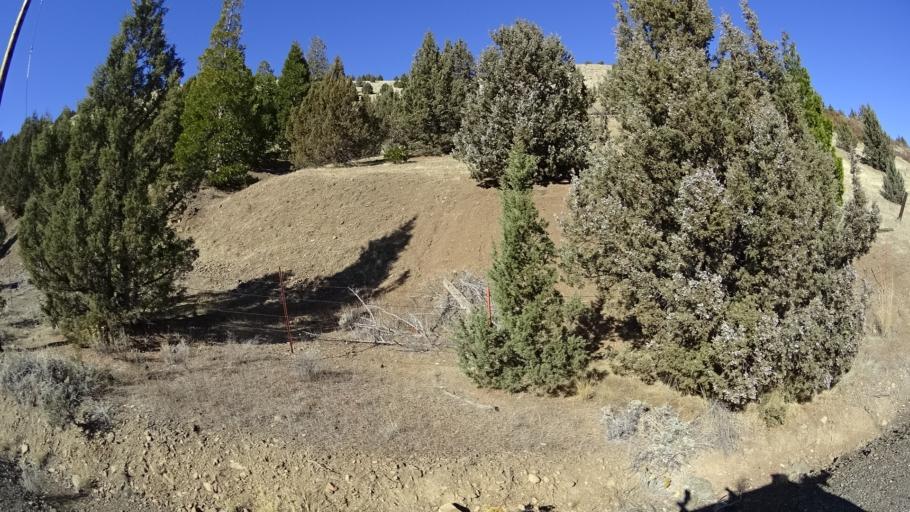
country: US
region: California
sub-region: Siskiyou County
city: Weed
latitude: 41.4868
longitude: -122.5681
